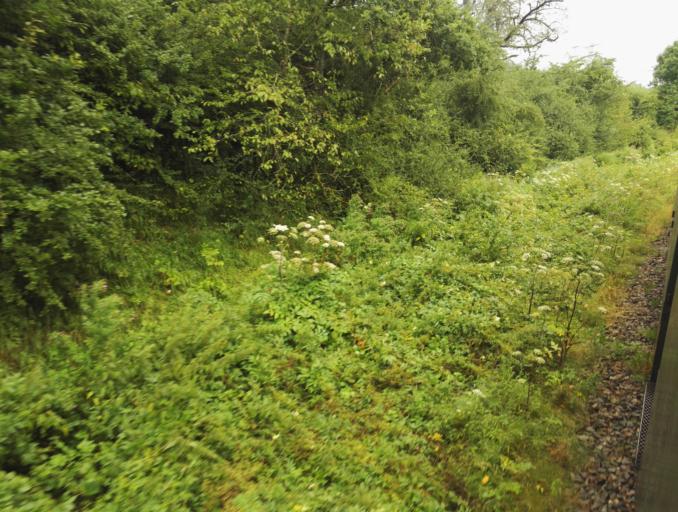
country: DE
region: Baden-Wuerttemberg
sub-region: Freiburg Region
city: Blumberg
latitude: 47.8151
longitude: 8.5425
